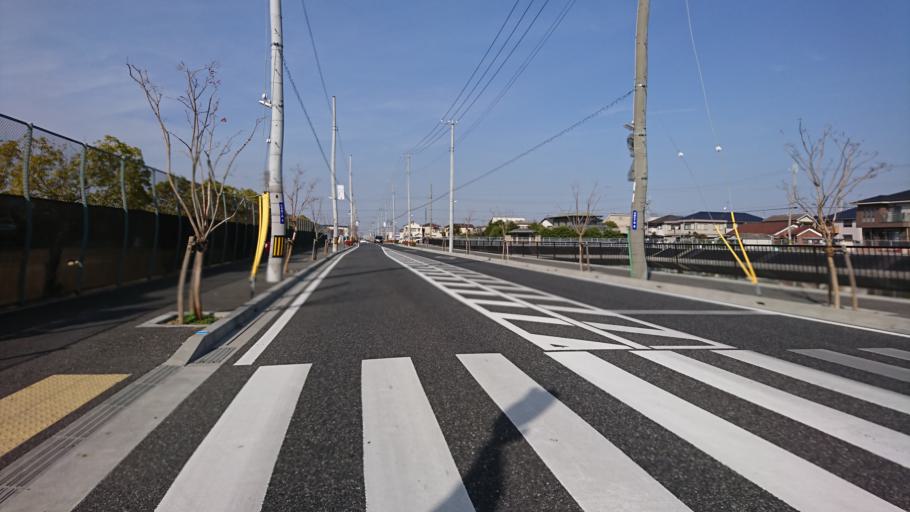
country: JP
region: Hyogo
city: Kakogawacho-honmachi
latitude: 34.7069
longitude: 134.8742
